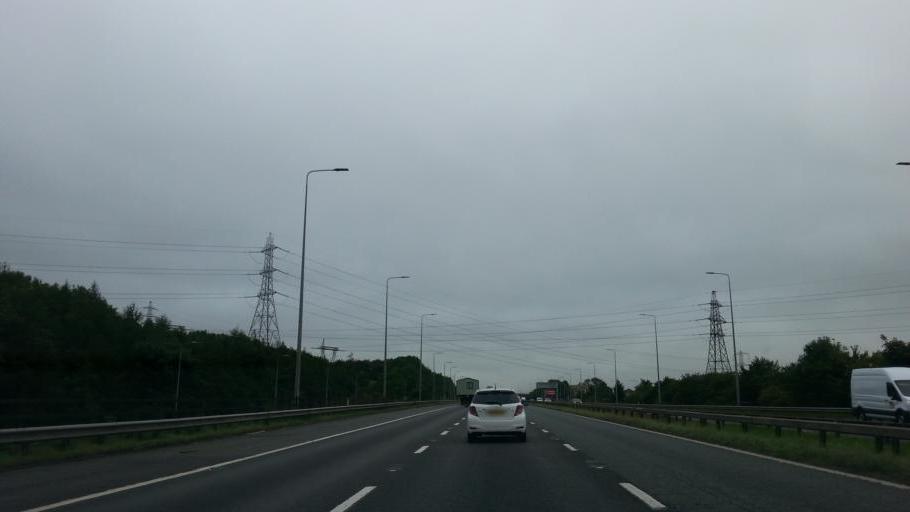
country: GB
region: England
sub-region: Calderdale
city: Elland
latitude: 53.6706
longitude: -1.8356
